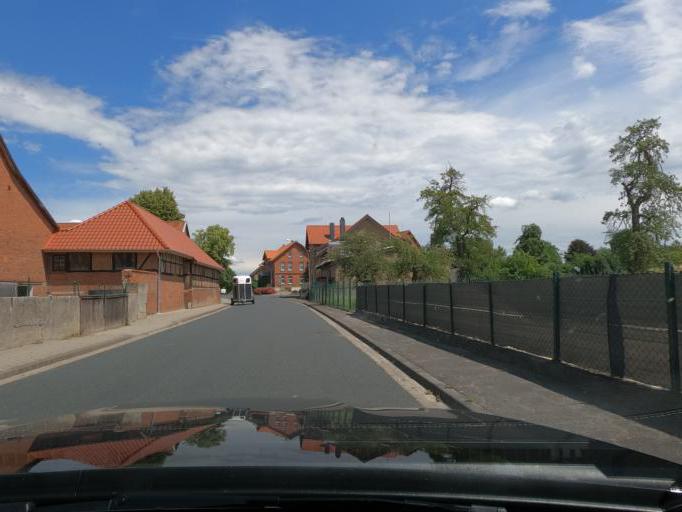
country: DE
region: Lower Saxony
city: Sohlde
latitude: 52.1893
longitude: 10.2358
